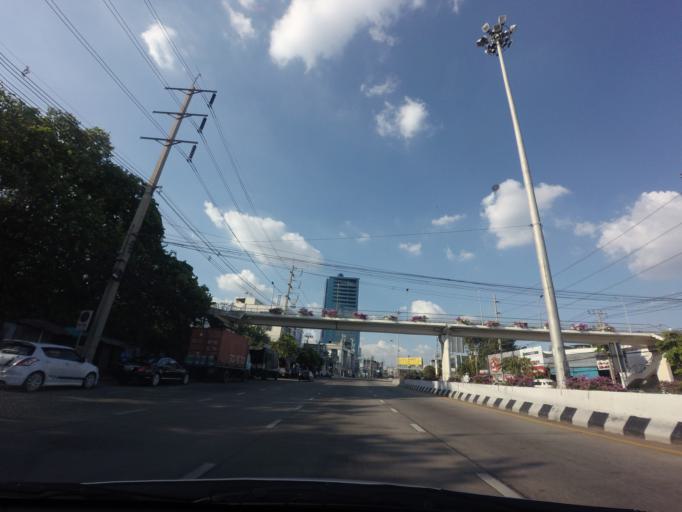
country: TH
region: Bangkok
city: Yan Nawa
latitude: 13.6986
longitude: 100.5458
